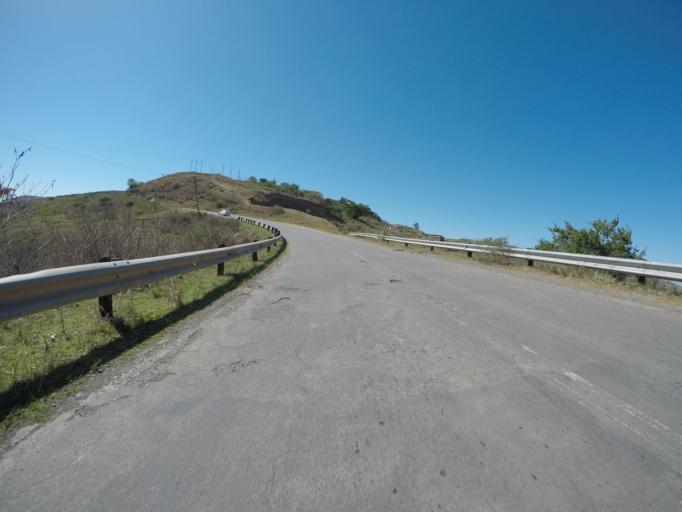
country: ZA
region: Eastern Cape
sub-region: OR Tambo District Municipality
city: Mthatha
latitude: -31.9155
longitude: 28.9622
